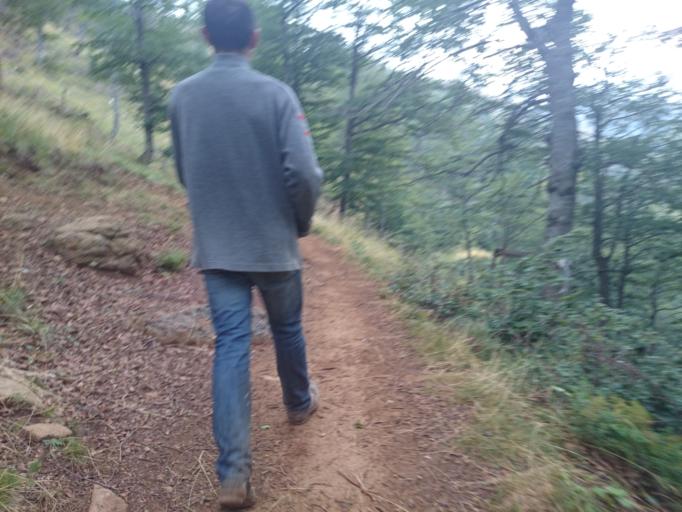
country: AL
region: Lezhe
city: Kurbnesh
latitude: 41.7850
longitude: 20.1498
